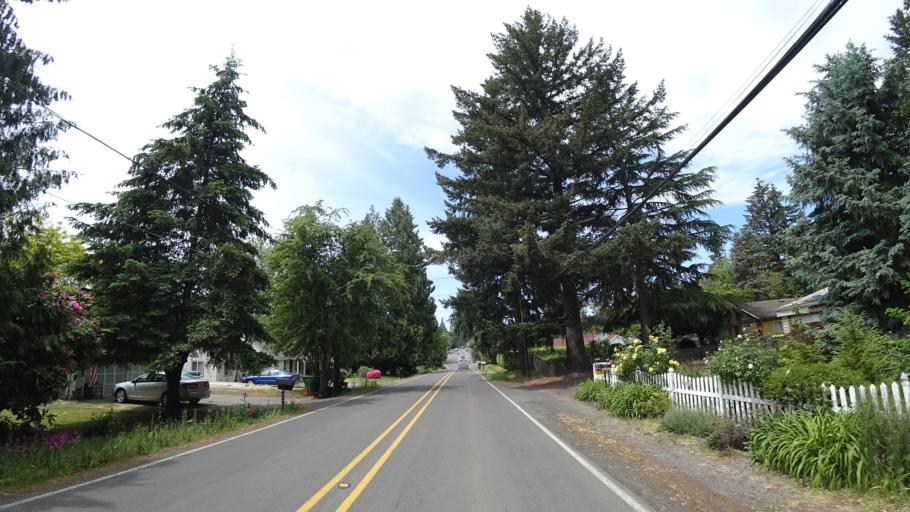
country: US
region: Oregon
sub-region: Washington County
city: Metzger
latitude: 45.4466
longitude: -122.7629
